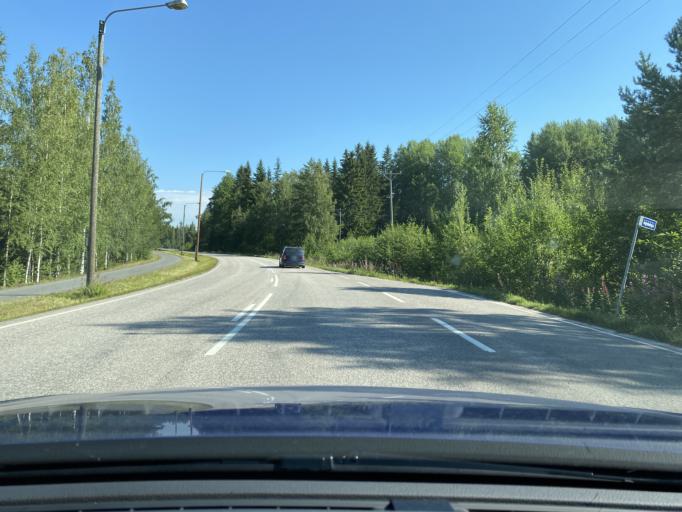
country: FI
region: Central Finland
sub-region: Jaemsae
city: Jaemsae
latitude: 61.8871
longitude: 25.3012
